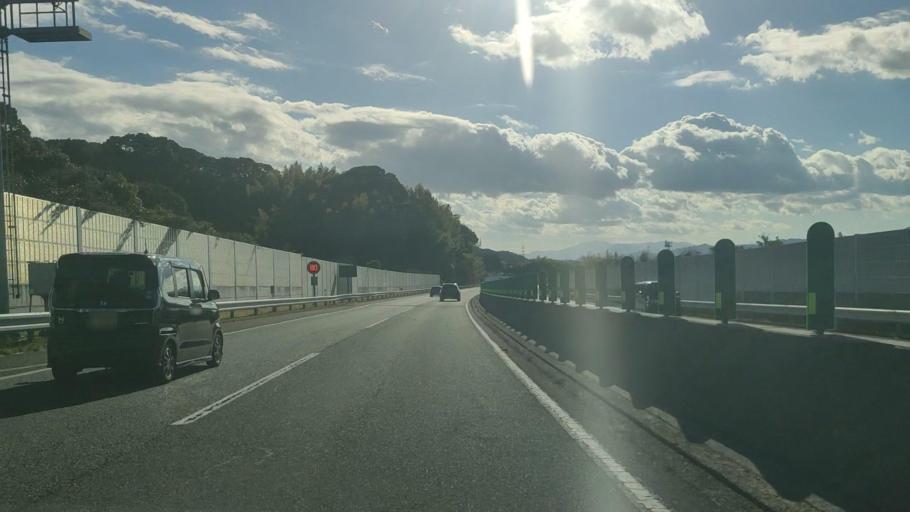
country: JP
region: Fukuoka
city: Nakama
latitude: 33.8287
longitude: 130.7650
